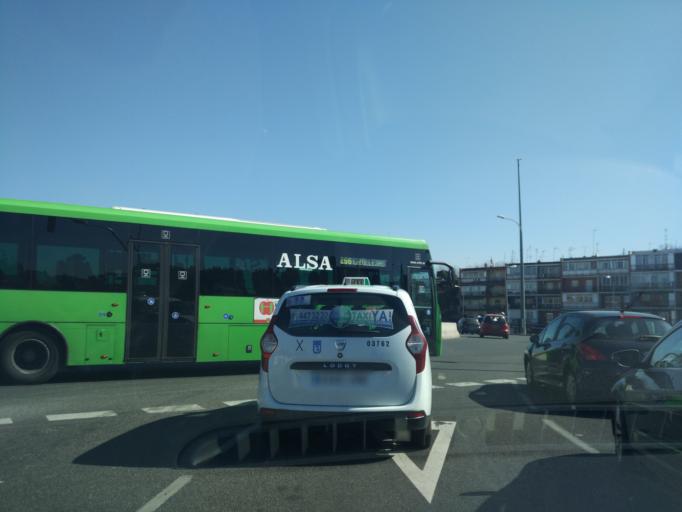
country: ES
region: Madrid
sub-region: Provincia de Madrid
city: San Blas
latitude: 40.4494
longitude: -3.6093
